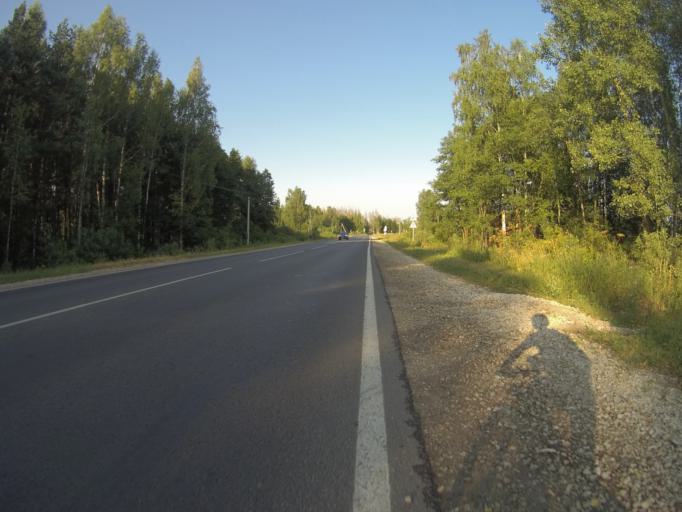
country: RU
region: Vladimir
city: Raduzhnyy
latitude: 56.0328
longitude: 40.3562
